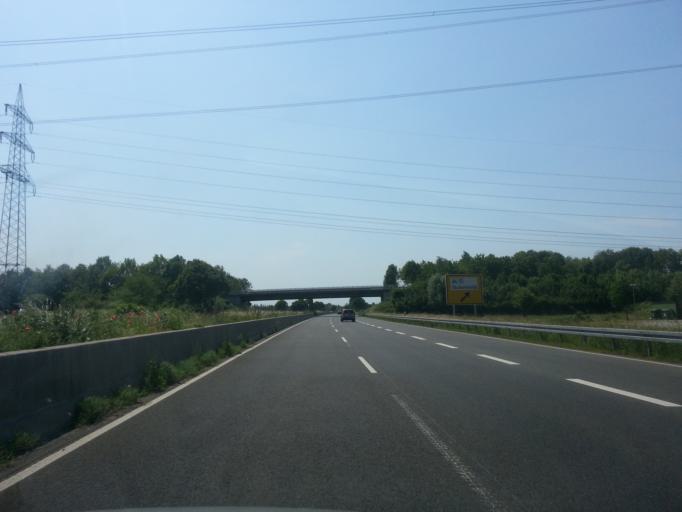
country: DE
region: Hesse
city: Lorsch
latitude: 49.6681
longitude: 8.5870
